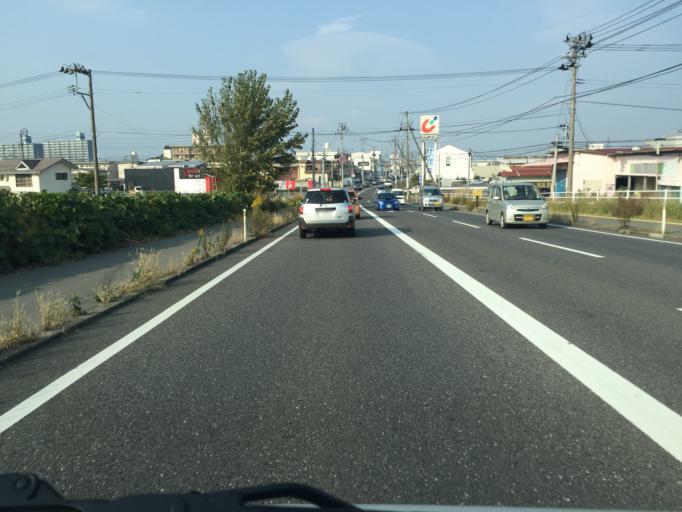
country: JP
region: Fukushima
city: Koriyama
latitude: 37.4037
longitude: 140.3961
